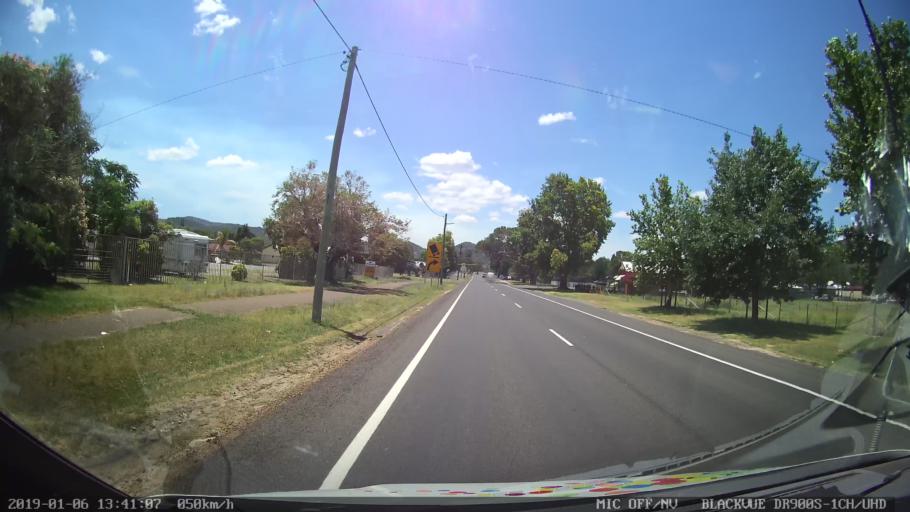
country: AU
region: New South Wales
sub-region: Tamworth Municipality
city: Kootingal
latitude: -31.0212
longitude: 151.0699
